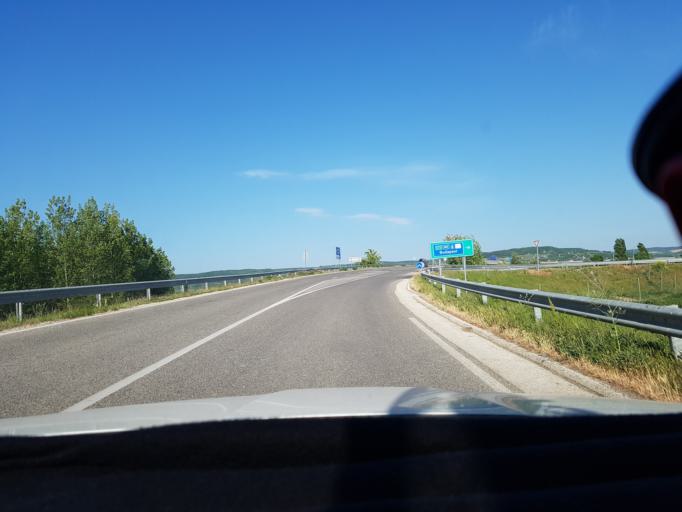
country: HU
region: Tolna
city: Ocseny
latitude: 46.3077
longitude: 18.7277
